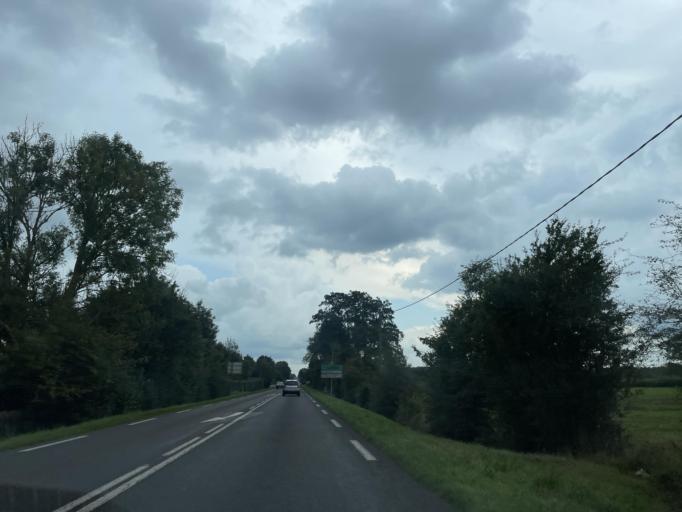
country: FR
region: Haute-Normandie
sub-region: Departement de la Seine-Maritime
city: Forges-les-Eaux
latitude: 49.6024
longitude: 1.5668
